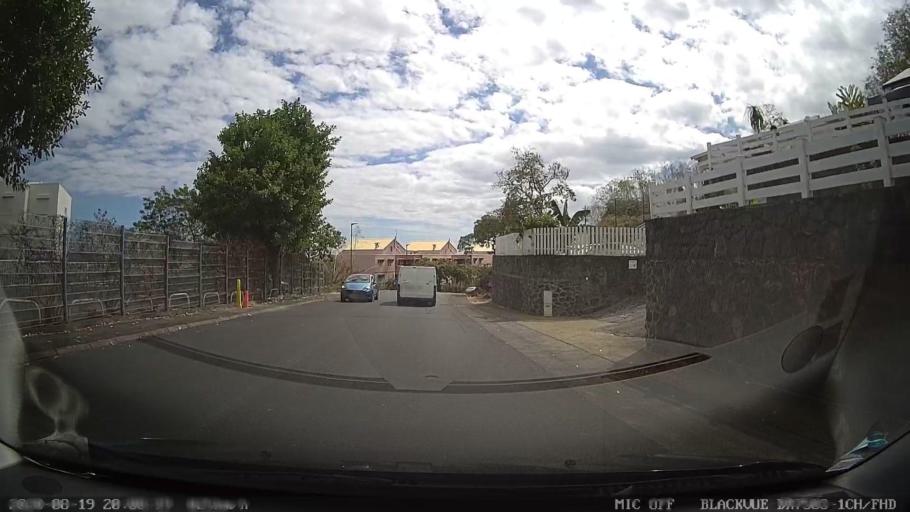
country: RE
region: Reunion
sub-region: Reunion
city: La Possession
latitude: -20.9538
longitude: 55.3321
